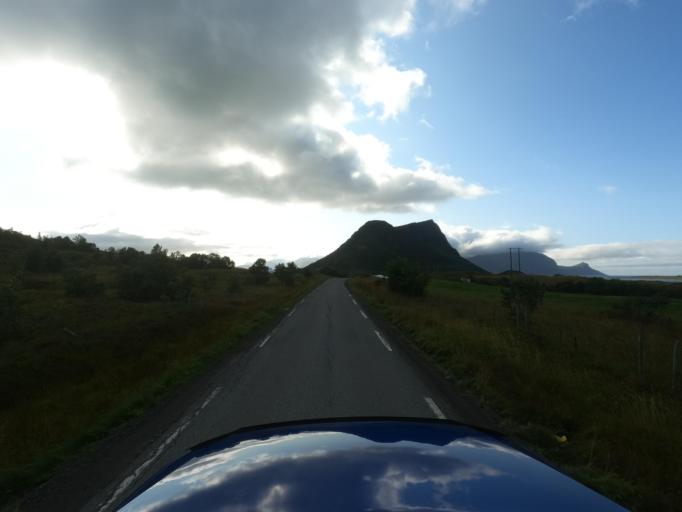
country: NO
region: Nordland
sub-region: Vestvagoy
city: Gravdal
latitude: 68.1705
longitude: 13.5580
